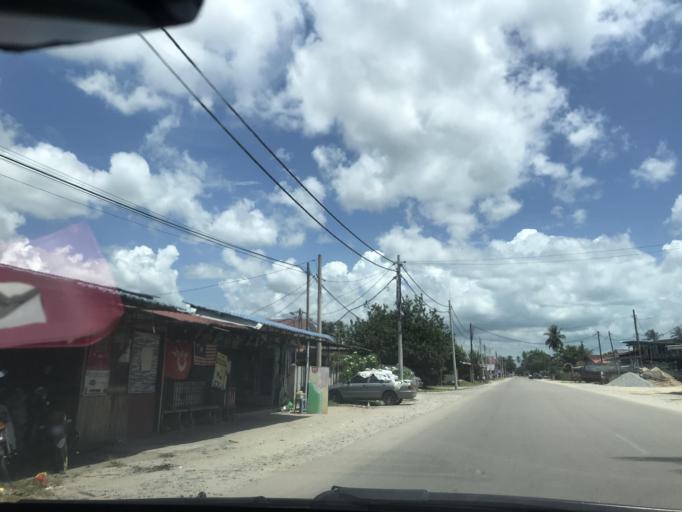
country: TH
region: Narathiwat
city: Tak Bai
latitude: 6.2276
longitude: 102.1002
